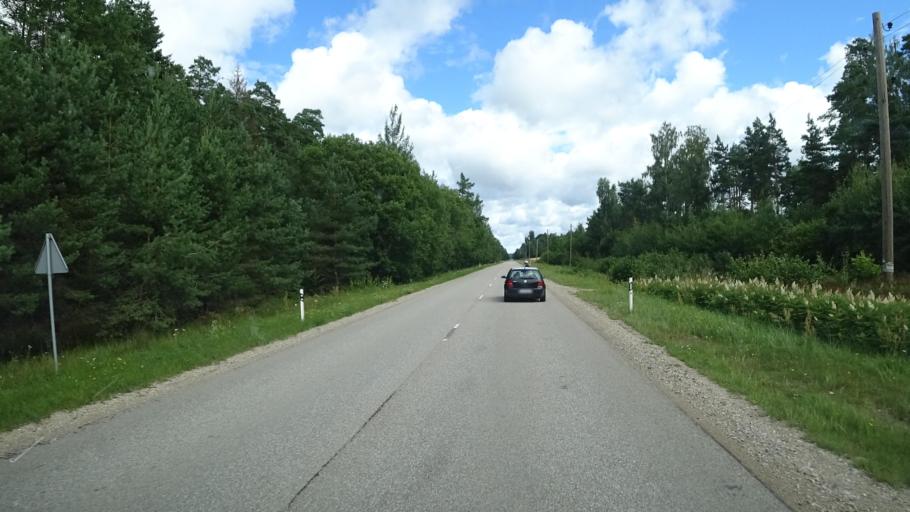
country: LV
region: Grobina
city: Grobina
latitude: 56.6961
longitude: 21.1624
